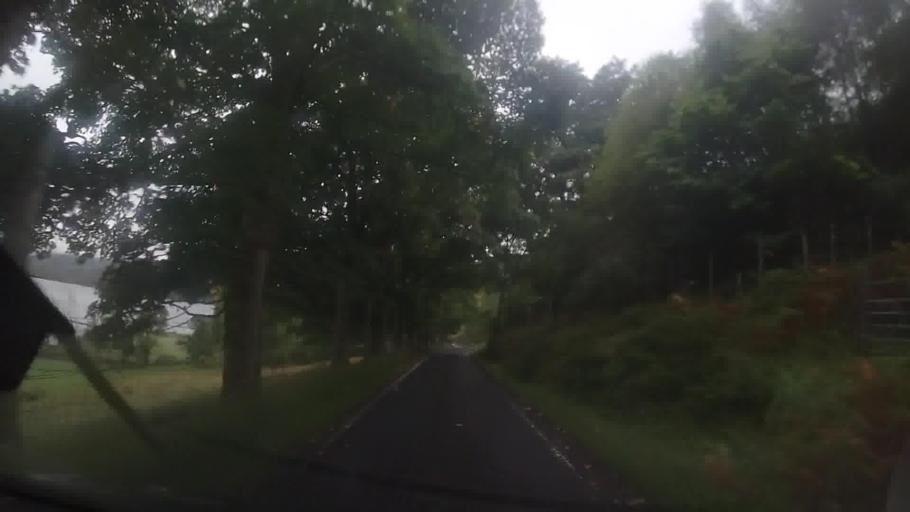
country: GB
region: Scotland
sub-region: Argyll and Bute
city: Isle Of Mull
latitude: 56.6821
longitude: -5.8646
